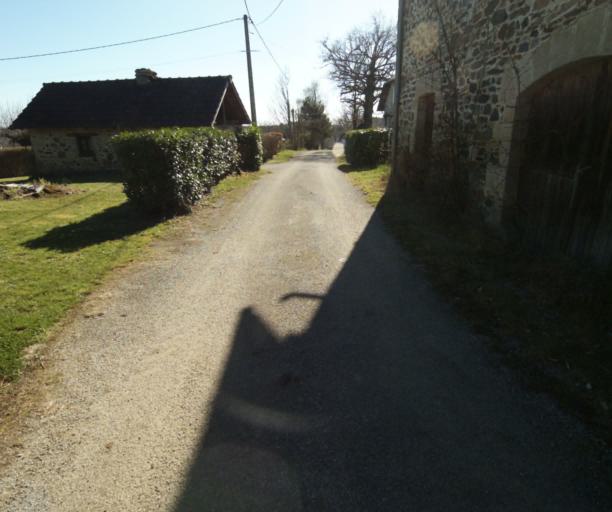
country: FR
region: Limousin
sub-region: Departement de la Correze
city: Chamboulive
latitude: 45.4401
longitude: 1.6739
